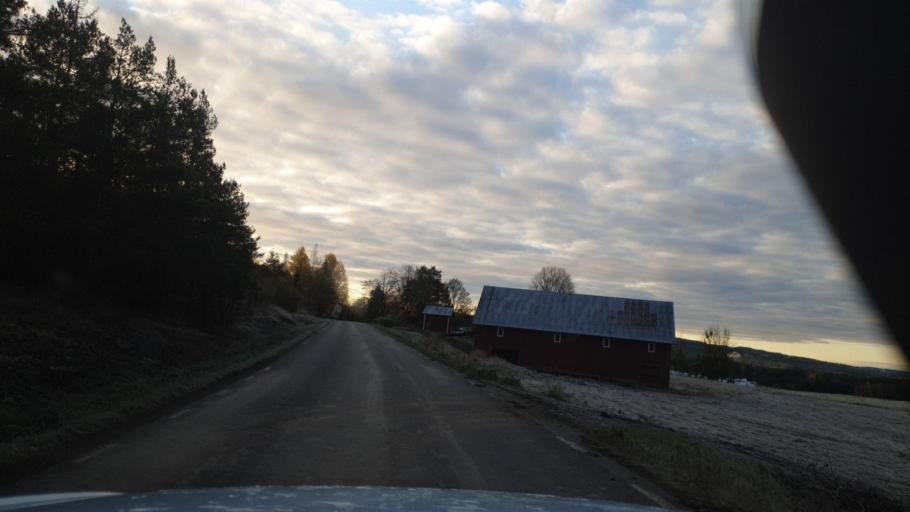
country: SE
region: Vaermland
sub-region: Eda Kommun
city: Charlottenberg
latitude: 59.7493
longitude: 12.1604
